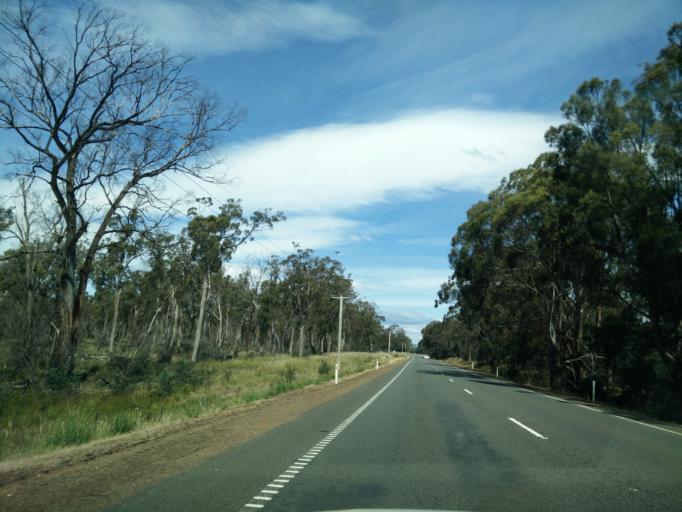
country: AU
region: Tasmania
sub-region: Northern Midlands
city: Evandale
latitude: -41.8231
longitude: 147.4276
